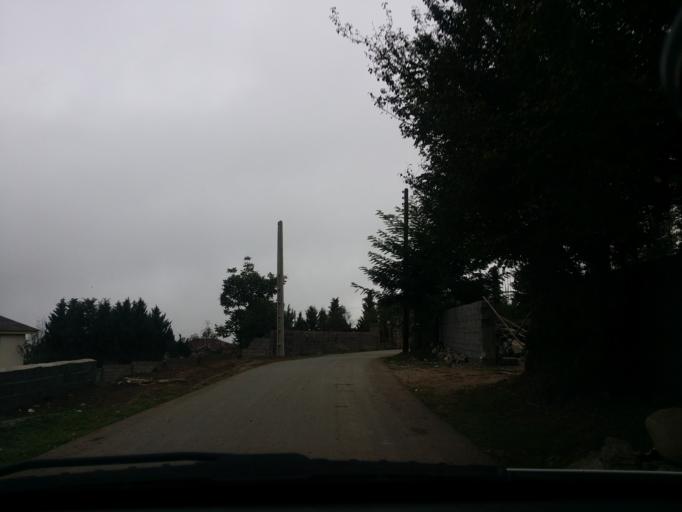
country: IR
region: Mazandaran
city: Chalus
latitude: 36.5108
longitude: 51.2290
